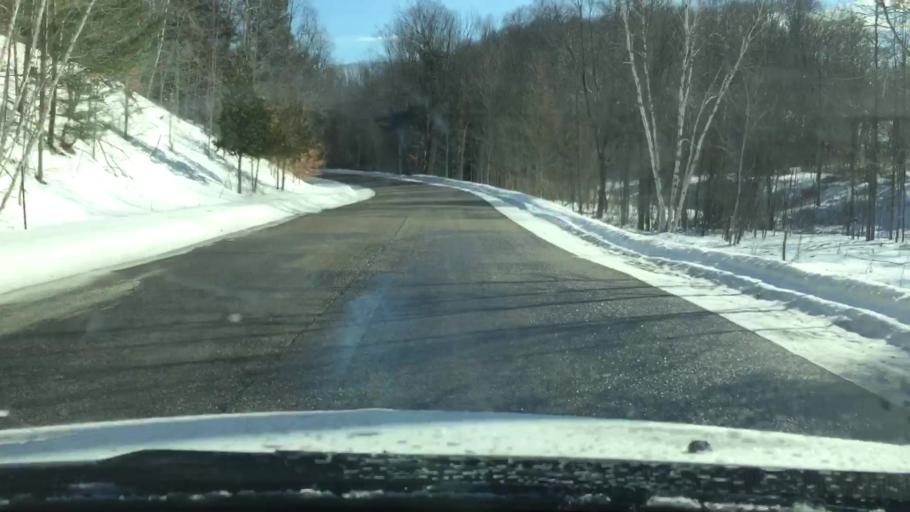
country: US
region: Michigan
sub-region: Charlevoix County
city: East Jordan
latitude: 45.1042
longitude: -85.1455
